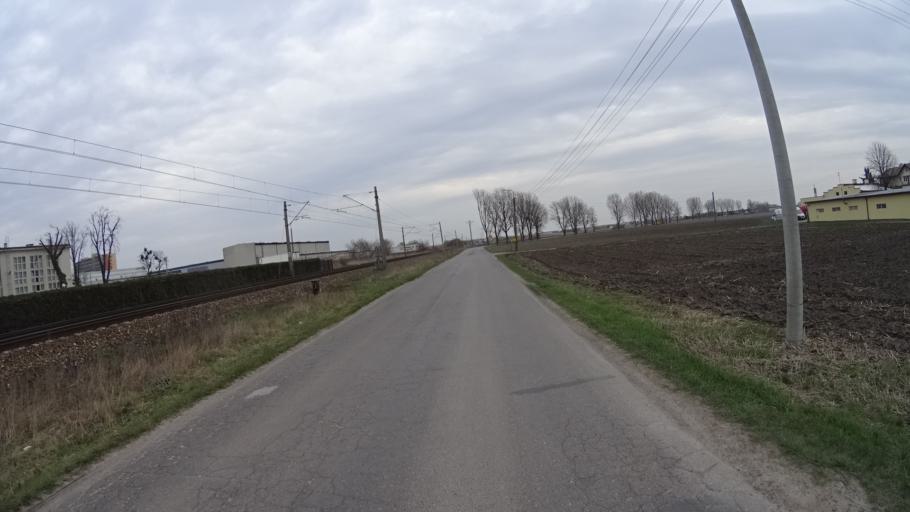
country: PL
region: Masovian Voivodeship
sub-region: Powiat warszawski zachodni
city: Ozarow Mazowiecki
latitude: 52.2068
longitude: 20.8158
